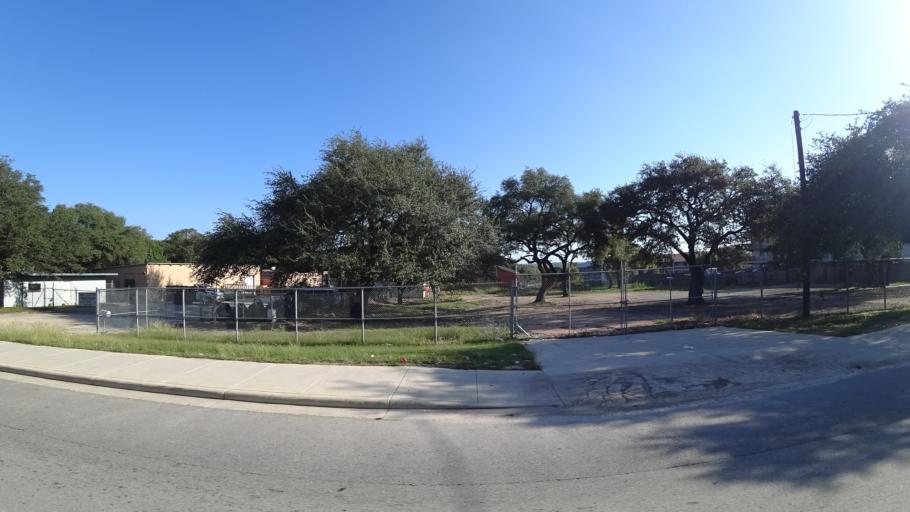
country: US
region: Texas
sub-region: Travis County
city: Austin
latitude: 30.3454
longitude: -97.6988
